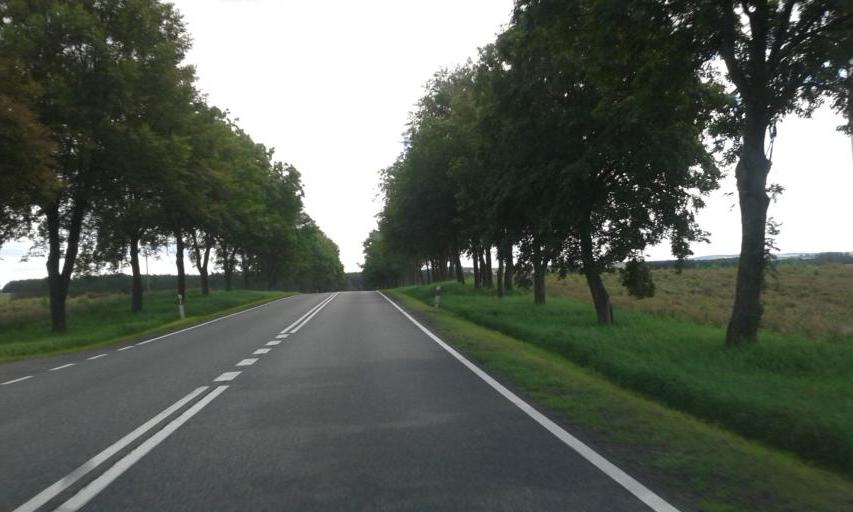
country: PL
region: West Pomeranian Voivodeship
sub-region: Powiat walecki
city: Walcz
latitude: 53.2520
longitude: 16.5229
